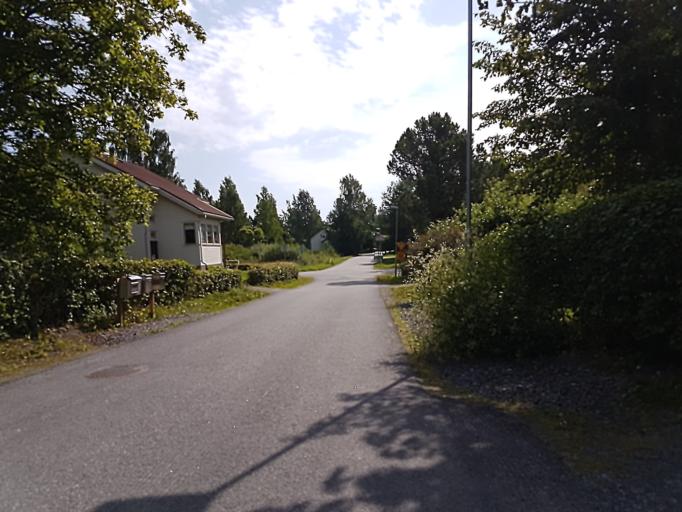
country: FI
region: Pirkanmaa
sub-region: Etelae-Pirkanmaa
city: Valkeakoski
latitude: 61.2519
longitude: 24.0430
